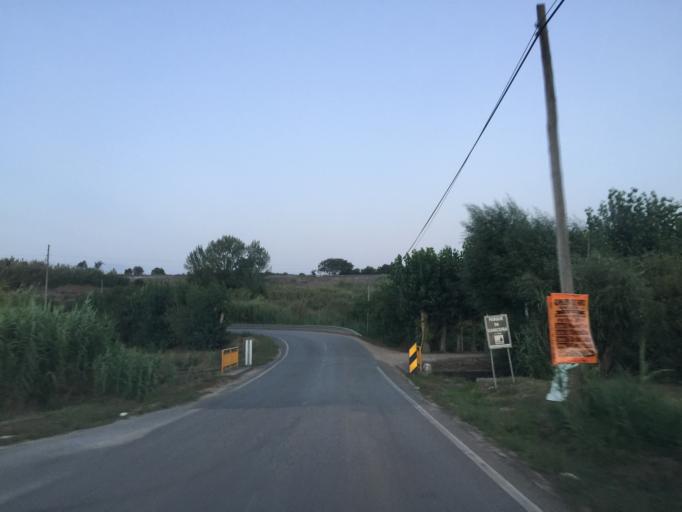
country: PT
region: Leiria
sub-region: Bombarral
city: Bombarral
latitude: 39.2722
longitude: -9.1694
